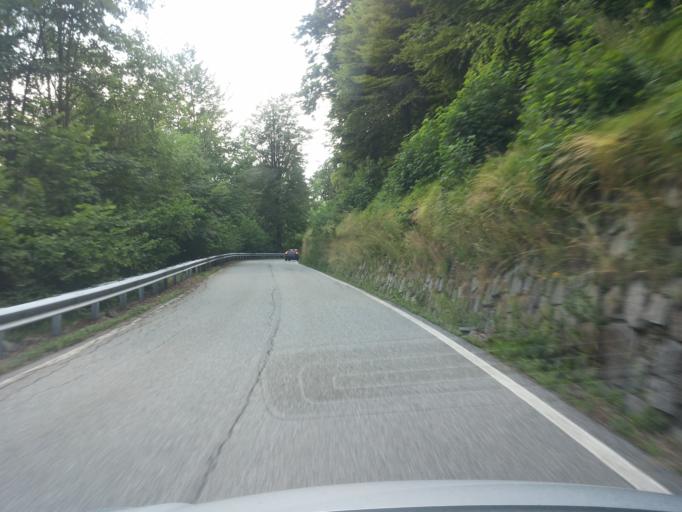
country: IT
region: Piedmont
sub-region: Provincia di Biella
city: Quittengo
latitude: 45.6634
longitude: 8.0220
